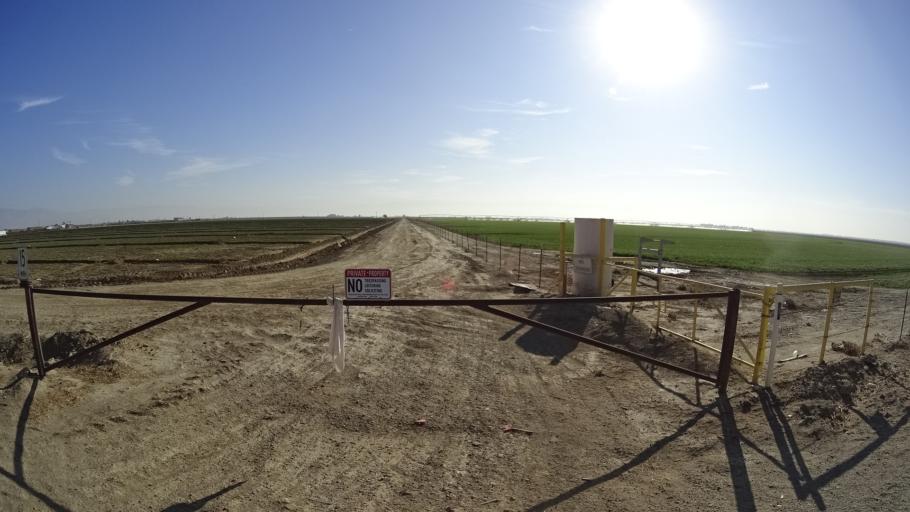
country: US
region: California
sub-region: Kern County
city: Lamont
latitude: 35.2959
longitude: -118.9454
